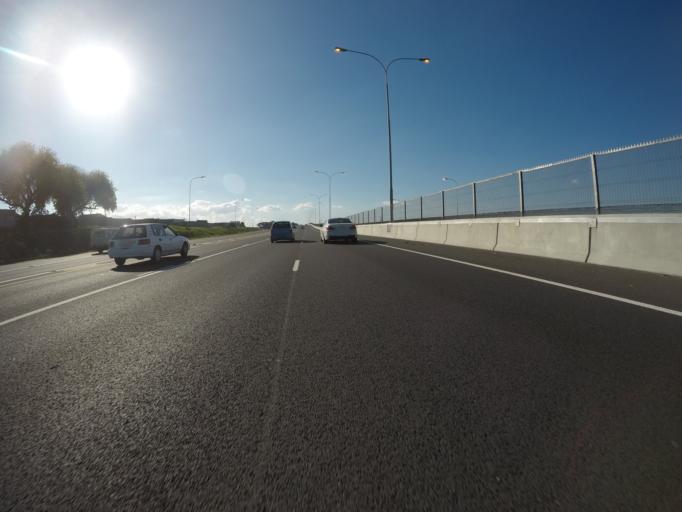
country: ZA
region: Western Cape
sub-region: City of Cape Town
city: Kraaifontein
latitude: -33.9591
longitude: 18.6567
